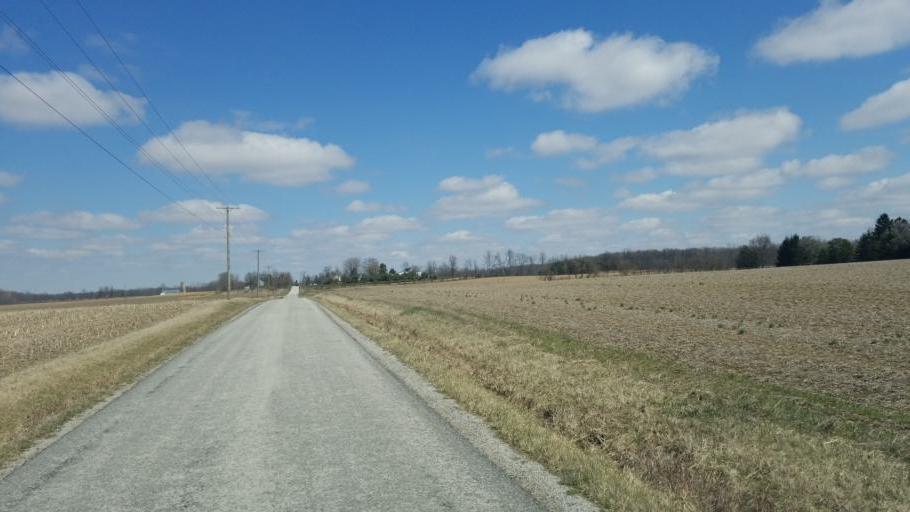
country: US
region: Ohio
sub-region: Crawford County
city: Galion
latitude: 40.7097
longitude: -82.8492
